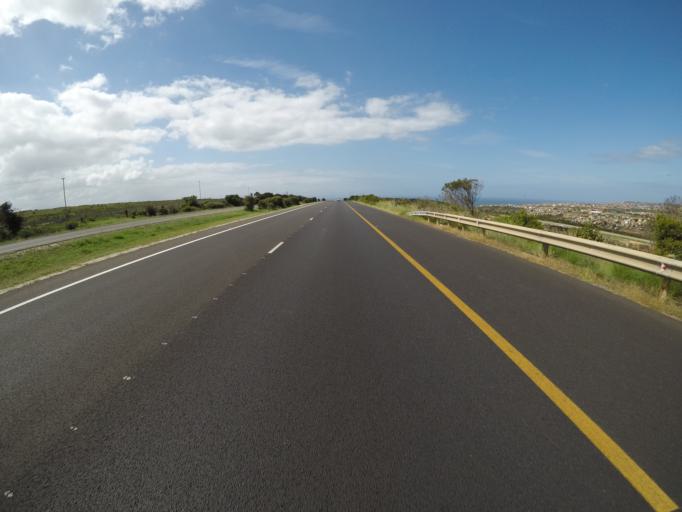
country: ZA
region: Western Cape
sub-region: Eden District Municipality
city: Mossel Bay
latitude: -34.1651
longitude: 22.0876
